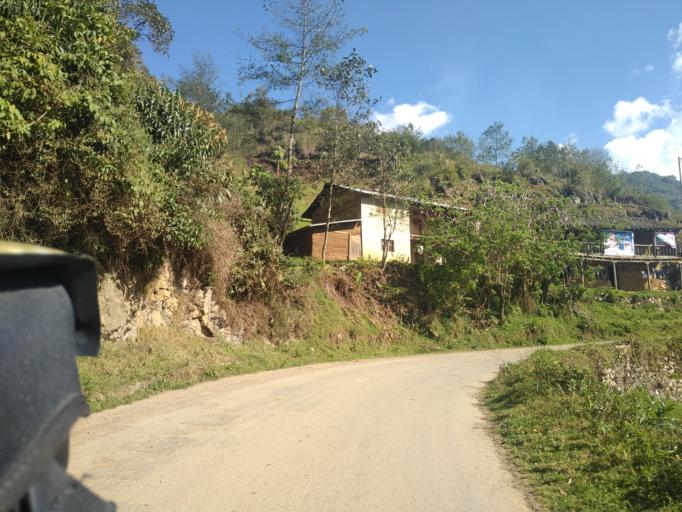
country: PE
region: Amazonas
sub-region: Provincia de Chachapoyas
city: Montevideo
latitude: -6.7168
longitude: -77.8206
